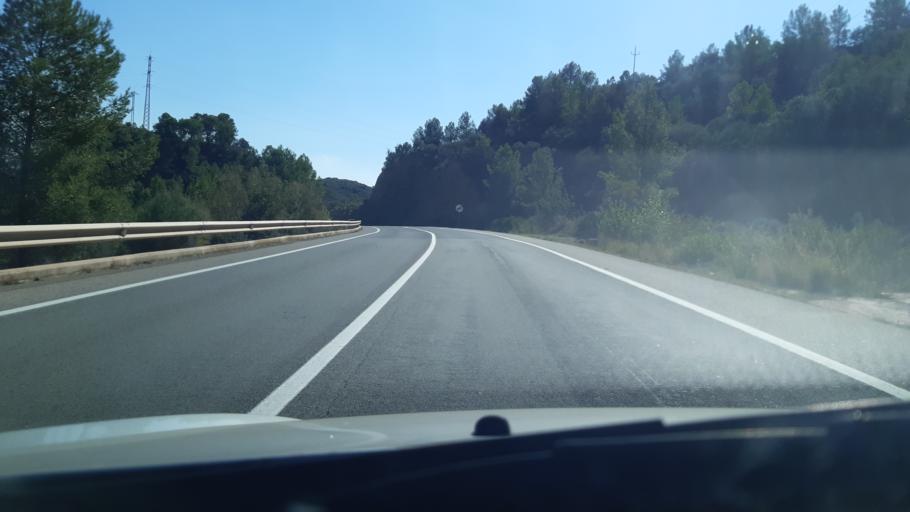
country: ES
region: Catalonia
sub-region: Provincia de Tarragona
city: Tivenys
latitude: 40.9268
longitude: 0.4865
